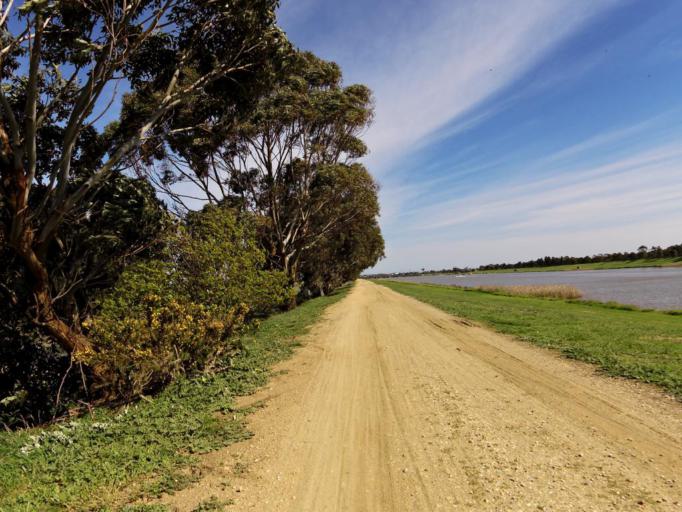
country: AU
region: Victoria
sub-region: Kingston
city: Patterson Lakes
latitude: -38.0531
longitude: 145.1593
